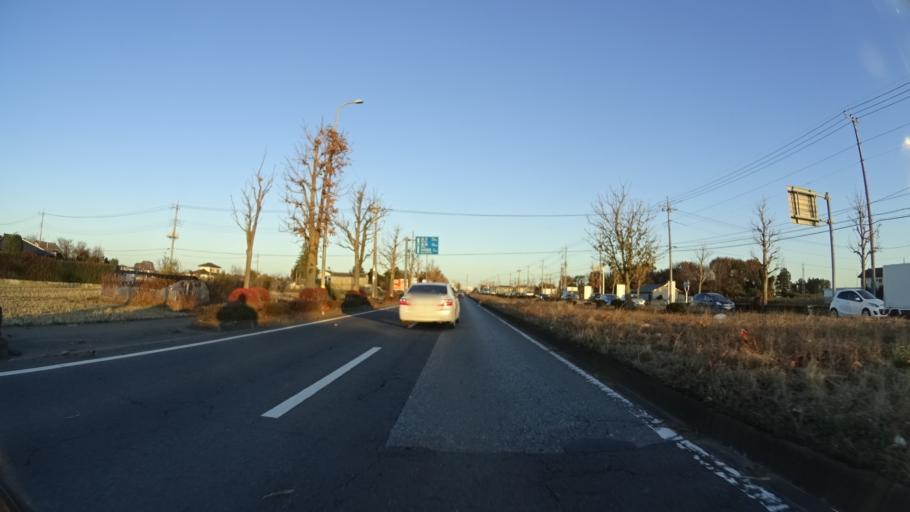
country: JP
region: Tochigi
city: Utsunomiya-shi
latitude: 36.5023
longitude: 139.8976
